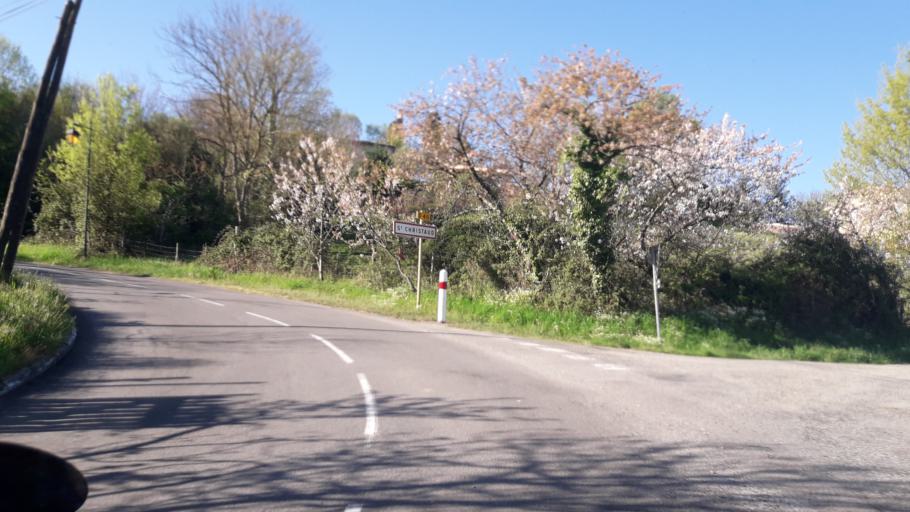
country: FR
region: Midi-Pyrenees
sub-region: Departement de la Haute-Garonne
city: Cazeres
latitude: 43.1905
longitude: 1.1284
